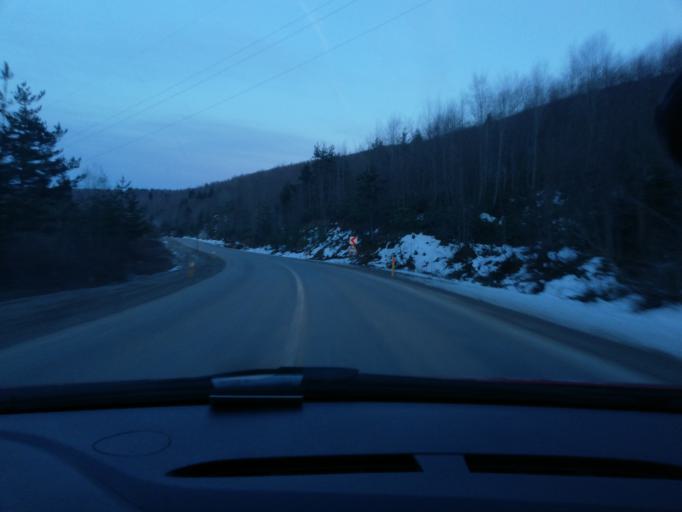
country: TR
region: Kastamonu
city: Inebolu
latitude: 41.8985
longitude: 33.7101
